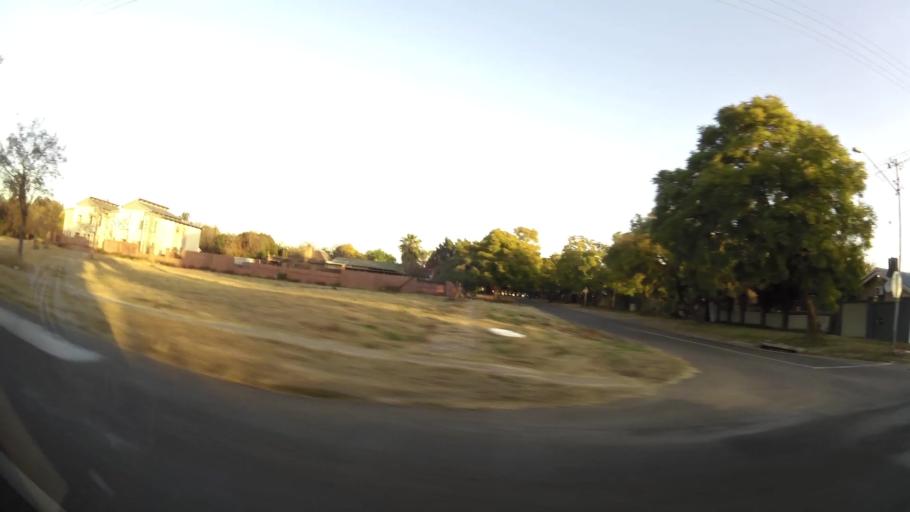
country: ZA
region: Gauteng
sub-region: City of Tshwane Metropolitan Municipality
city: Pretoria
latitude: -25.7116
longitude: 28.2224
